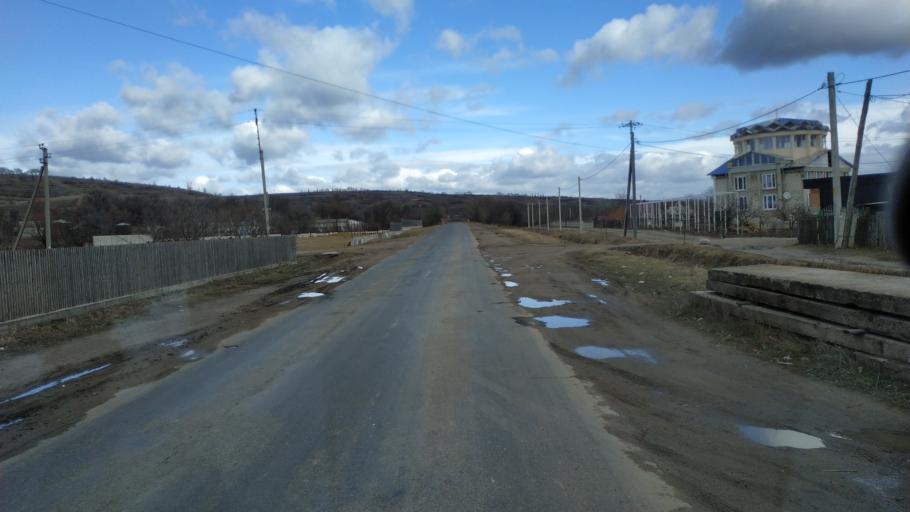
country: MD
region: Stinga Nistrului
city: Bucovat
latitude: 47.1605
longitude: 28.4340
